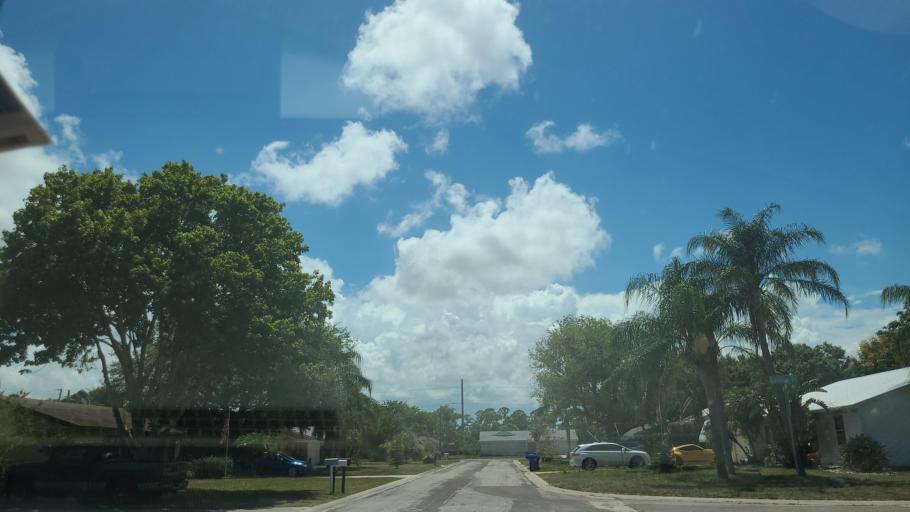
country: US
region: Florida
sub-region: Indian River County
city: Sebastian
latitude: 27.7804
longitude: -80.4683
